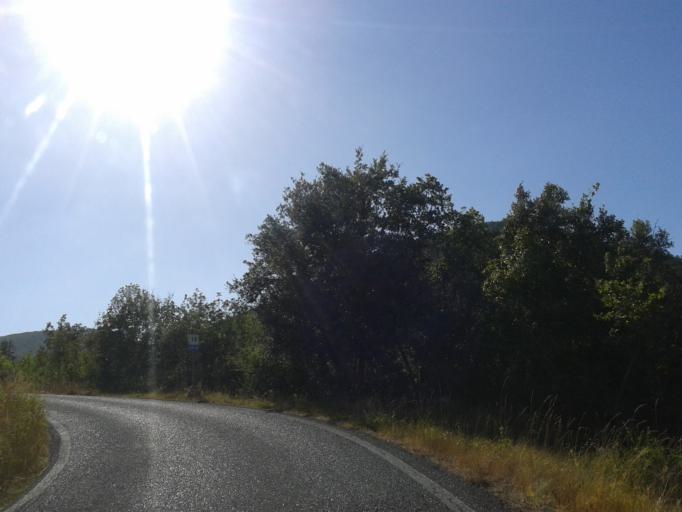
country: IT
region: Tuscany
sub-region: Province of Pisa
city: Chianni
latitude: 43.4570
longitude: 10.6287
